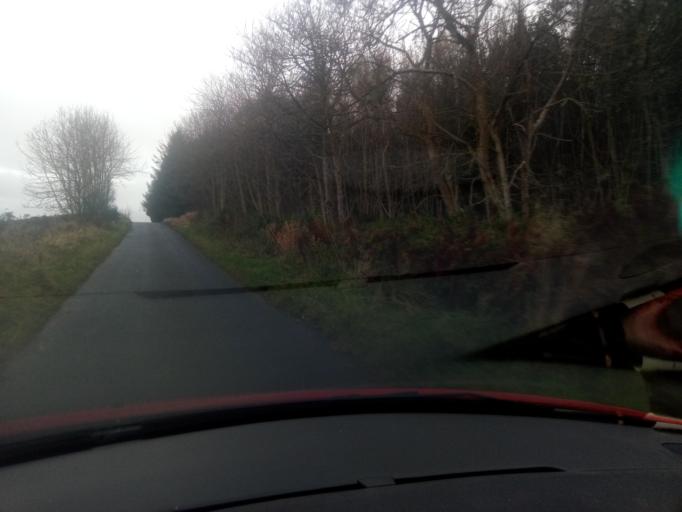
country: GB
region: Scotland
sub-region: The Scottish Borders
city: Jedburgh
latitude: 55.4842
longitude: -2.5862
